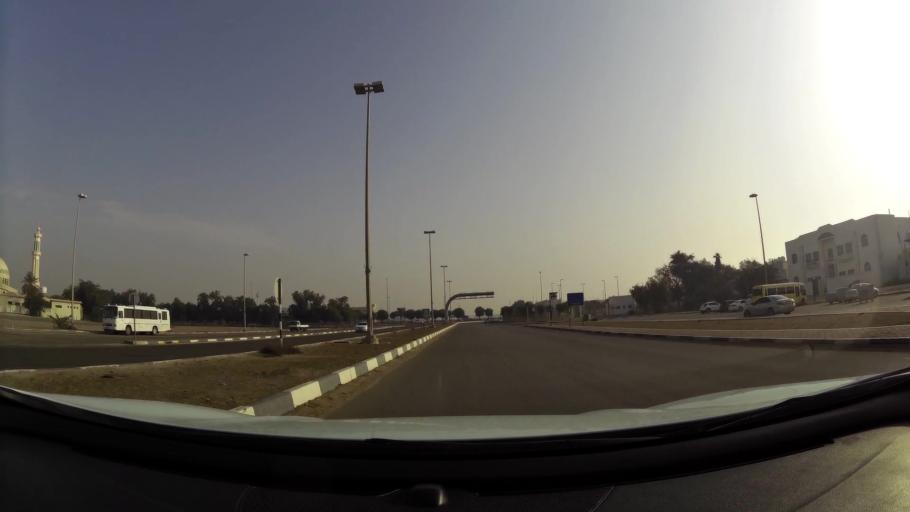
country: AE
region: Abu Dhabi
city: Abu Dhabi
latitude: 24.2939
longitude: 54.6277
